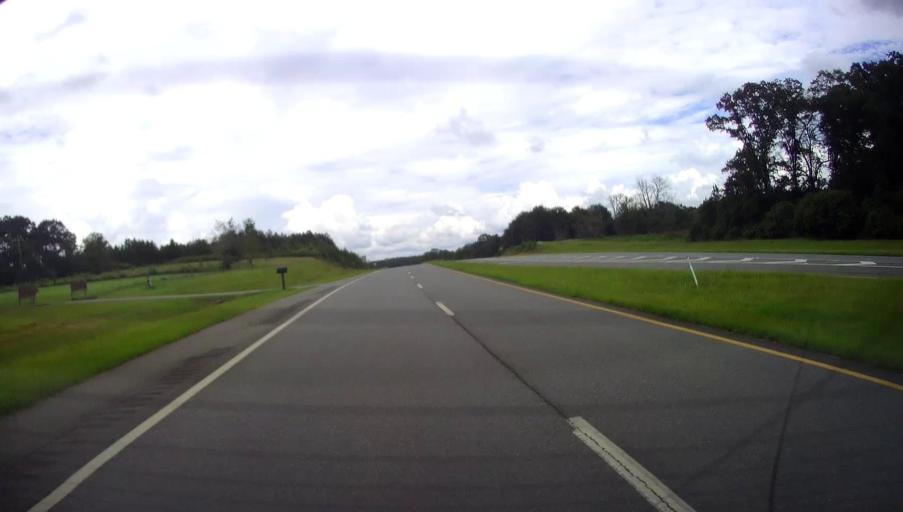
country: US
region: Georgia
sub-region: Schley County
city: Ellaville
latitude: 32.2676
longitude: -84.3030
